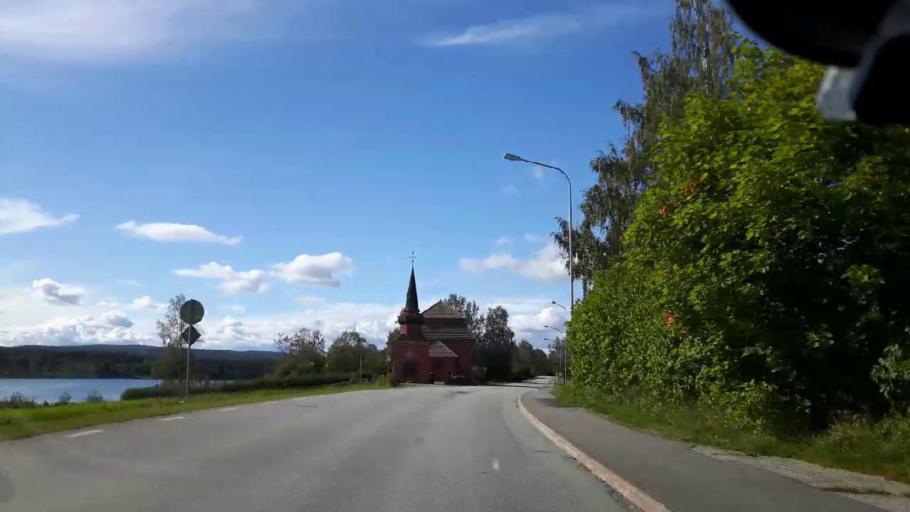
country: SE
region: Jaemtland
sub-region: Braecke Kommun
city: Braecke
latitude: 63.1680
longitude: 15.5867
